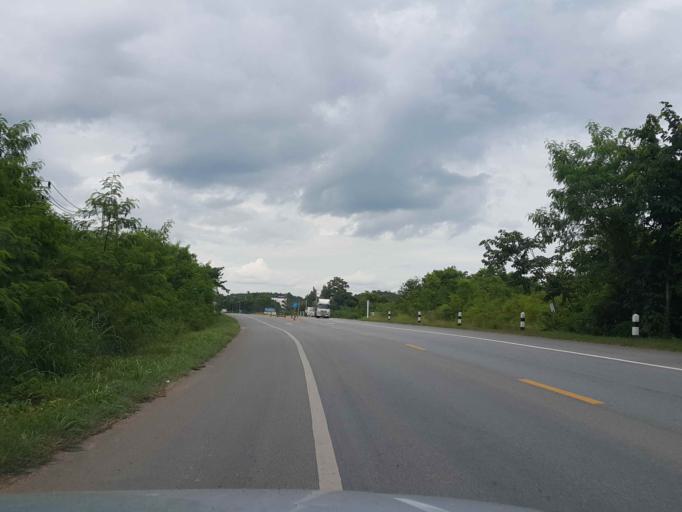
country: TH
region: Lampang
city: Lampang
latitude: 18.2534
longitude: 99.5390
